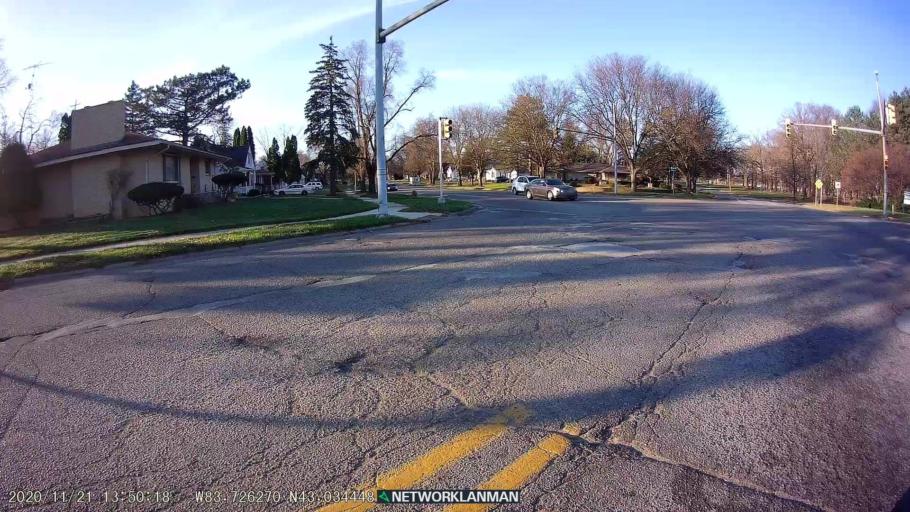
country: US
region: Michigan
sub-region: Genesee County
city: Flint
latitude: 43.0344
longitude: -83.7263
